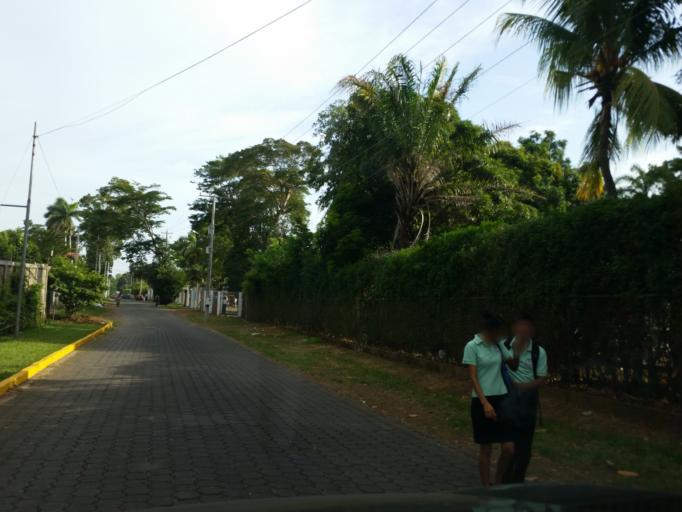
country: NI
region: Managua
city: Managua
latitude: 12.0950
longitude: -86.2330
